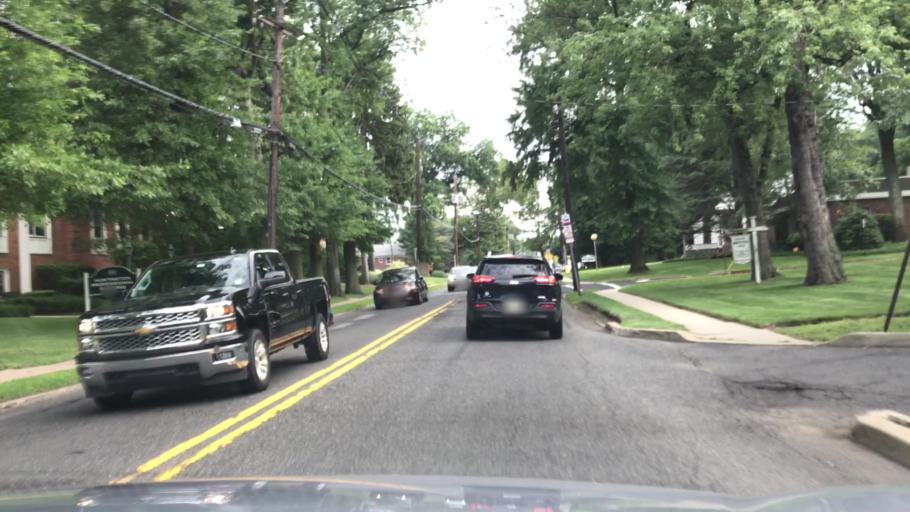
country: US
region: New Jersey
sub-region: Bergen County
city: Oradell
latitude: 40.9577
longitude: -74.0309
